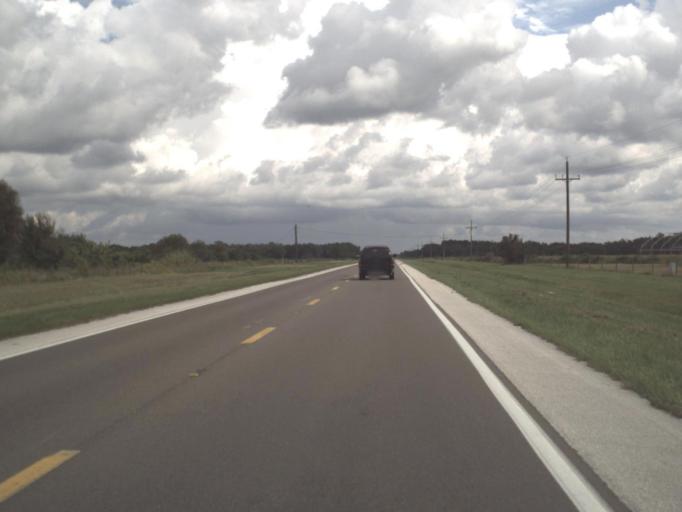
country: US
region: Florida
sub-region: Hendry County
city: LaBelle
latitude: 26.7996
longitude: -81.4239
